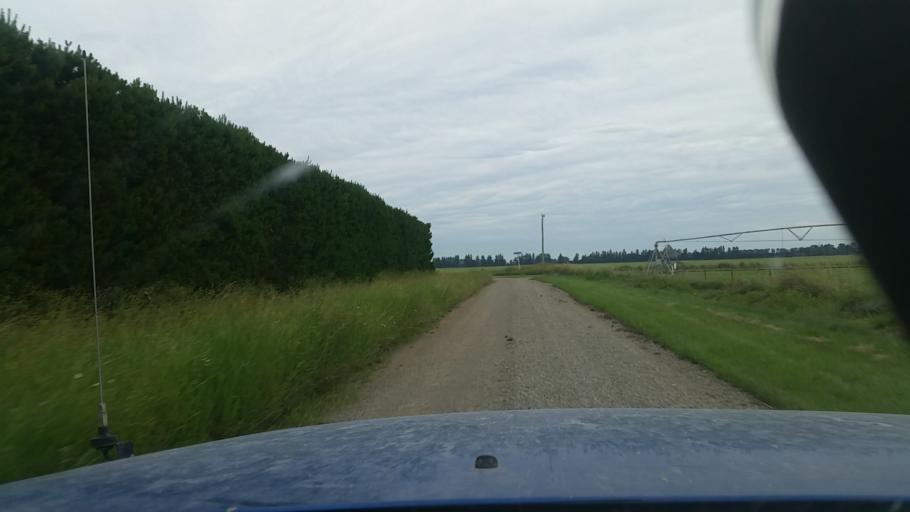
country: NZ
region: Canterbury
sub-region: Ashburton District
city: Tinwald
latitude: -43.9507
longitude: 171.5711
